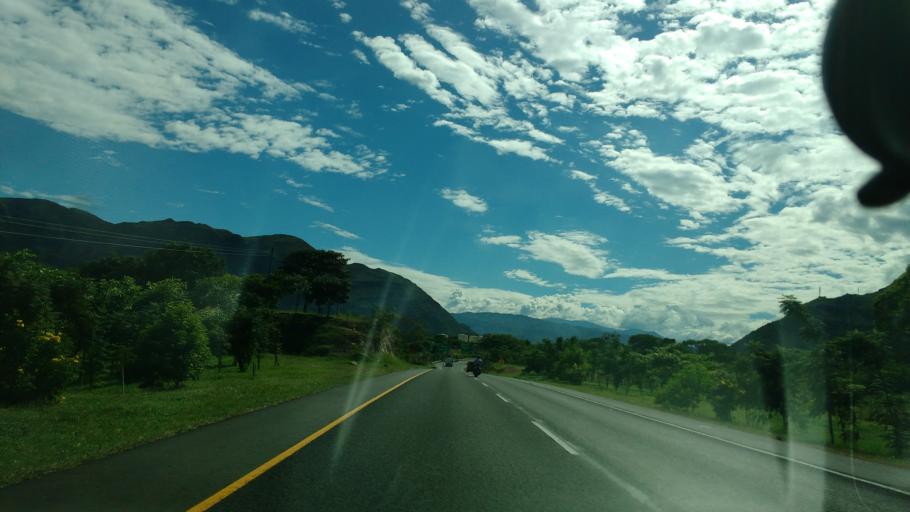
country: CO
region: Tolima
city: Valle de San Juan
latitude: 4.2778
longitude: -75.0092
